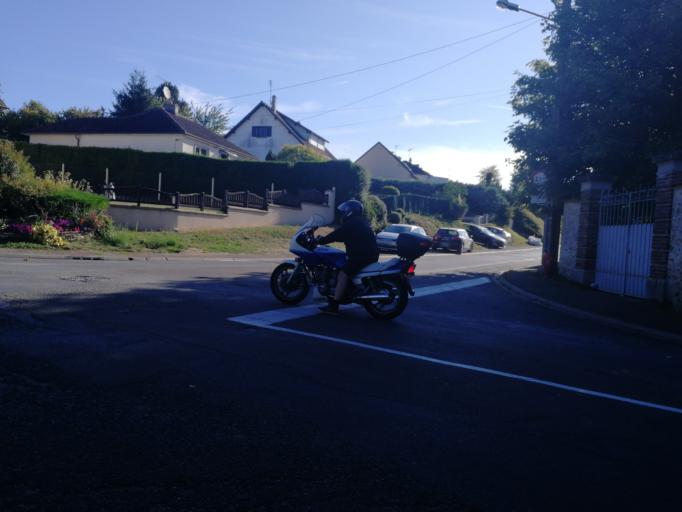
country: FR
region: Centre
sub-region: Departement d'Eure-et-Loir
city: Gallardon
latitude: 48.5288
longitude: 1.6741
